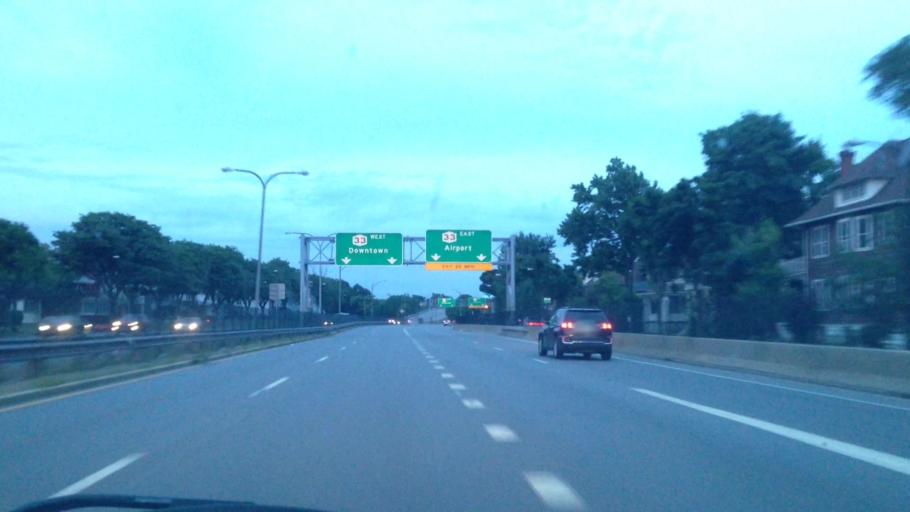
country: US
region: New York
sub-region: Erie County
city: Kenmore
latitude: 42.9263
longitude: -78.8483
